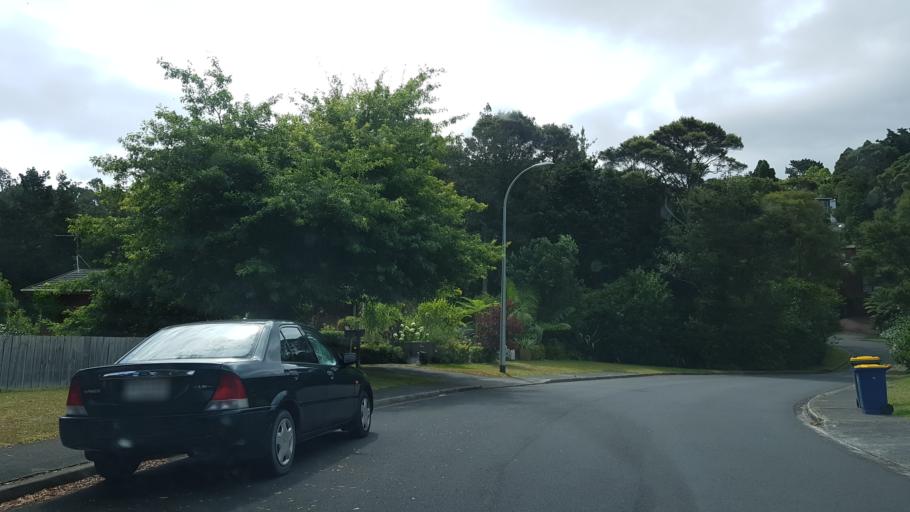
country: NZ
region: Auckland
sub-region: Auckland
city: North Shore
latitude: -36.7703
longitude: 174.7173
